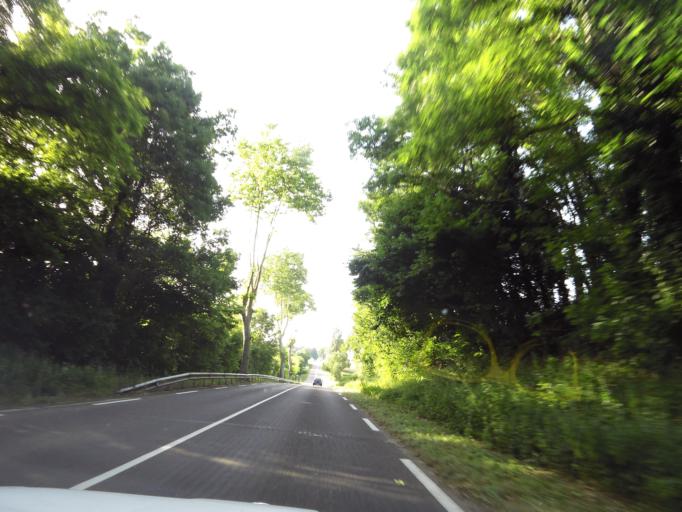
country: FR
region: Rhone-Alpes
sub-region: Departement de l'Ain
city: Meximieux
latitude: 45.9220
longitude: 5.1888
